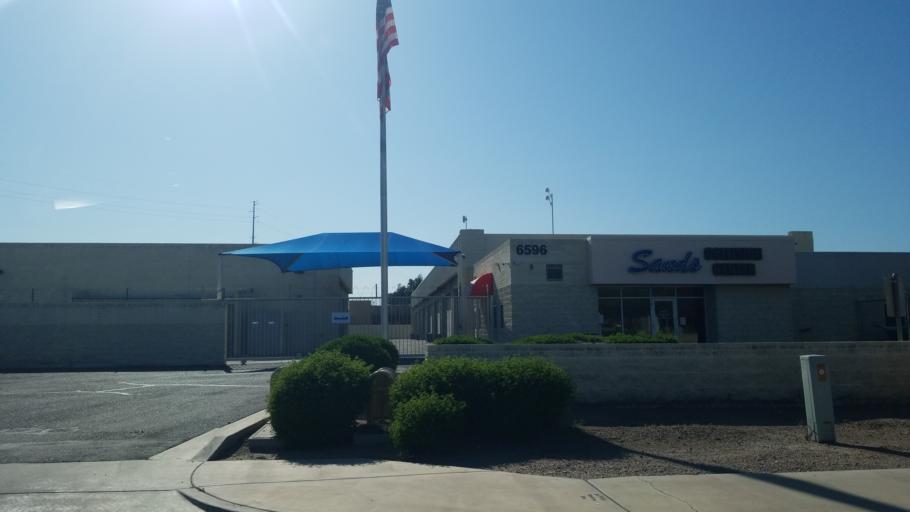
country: US
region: Arizona
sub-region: Maricopa County
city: Glendale
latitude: 33.5324
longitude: -112.1750
